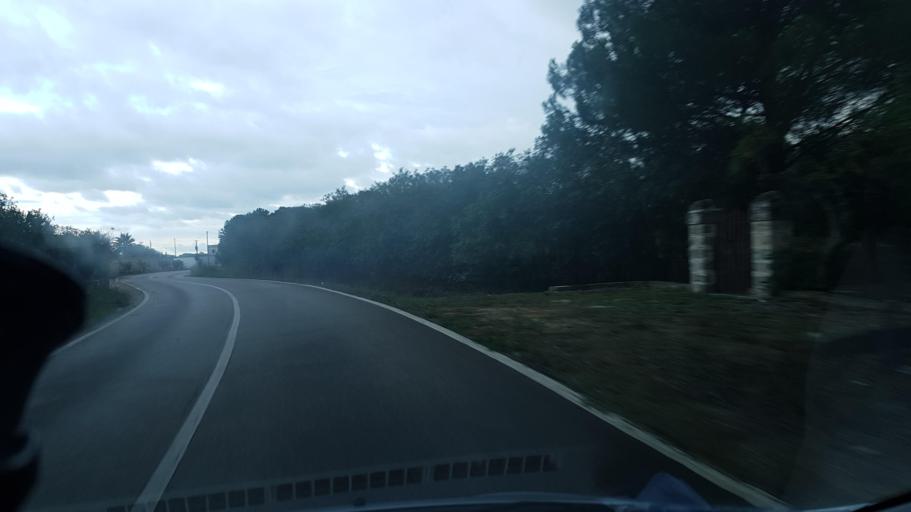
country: IT
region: Apulia
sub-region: Provincia di Lecce
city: Novoli
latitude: 40.3591
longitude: 18.0594
